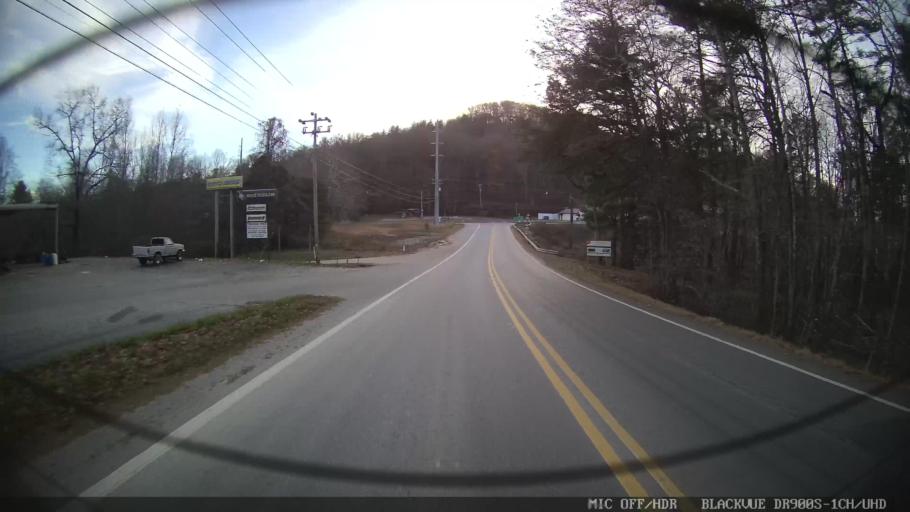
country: US
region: Georgia
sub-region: Union County
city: Blairsville
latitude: 34.8708
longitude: -83.9521
